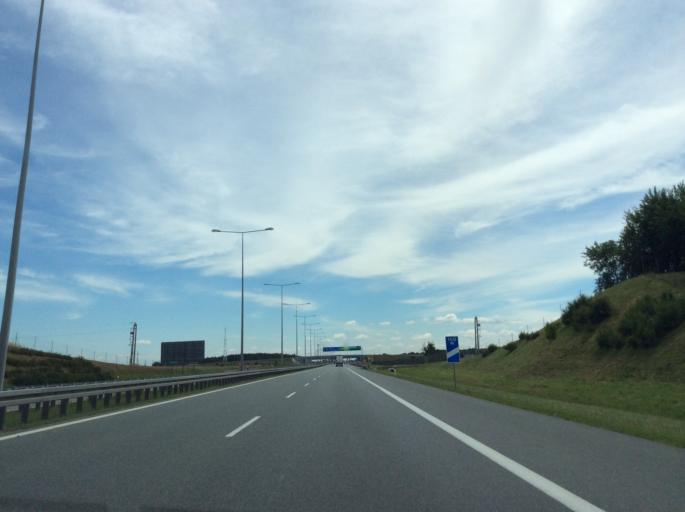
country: PL
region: Greater Poland Voivodeship
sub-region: Powiat poznanski
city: Buk
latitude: 52.3800
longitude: 16.5545
